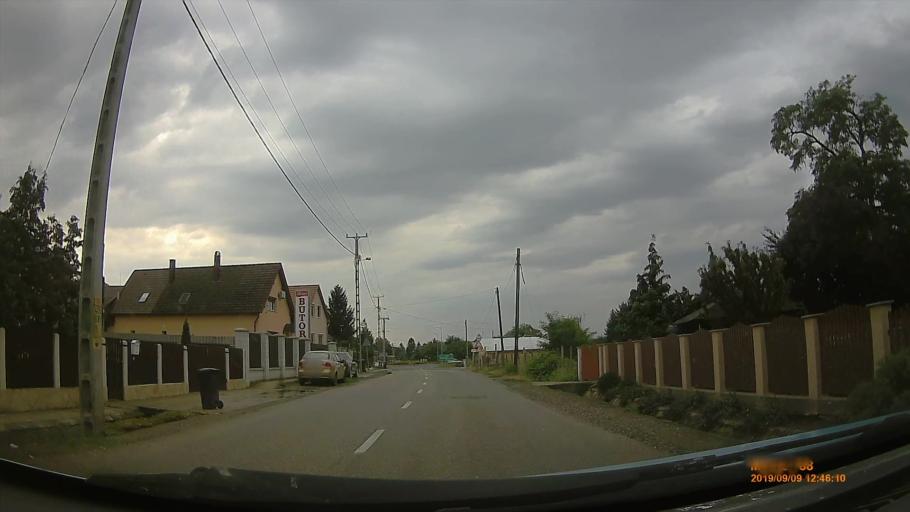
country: HU
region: Szabolcs-Szatmar-Bereg
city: Nyirpazony
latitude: 47.9503
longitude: 21.8047
